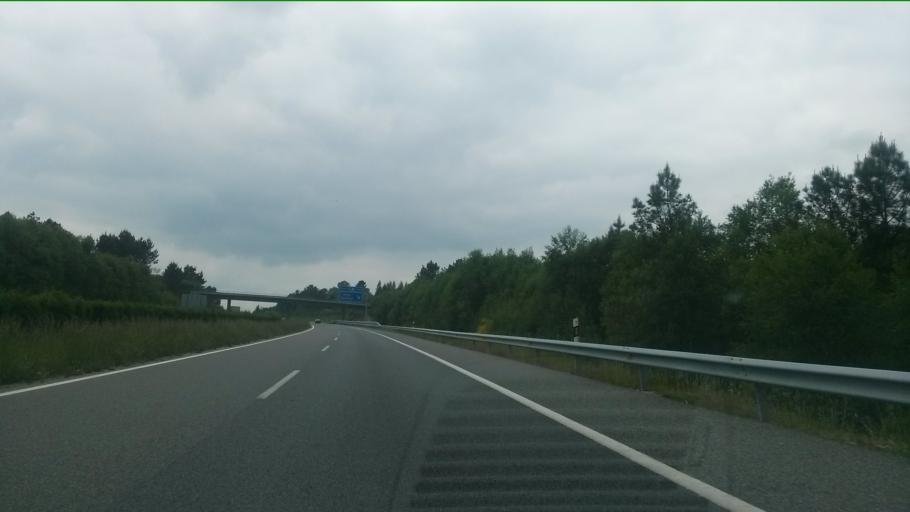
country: ES
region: Galicia
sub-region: Provincia de Lugo
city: Guitiriz
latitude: 43.1907
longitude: -7.9371
